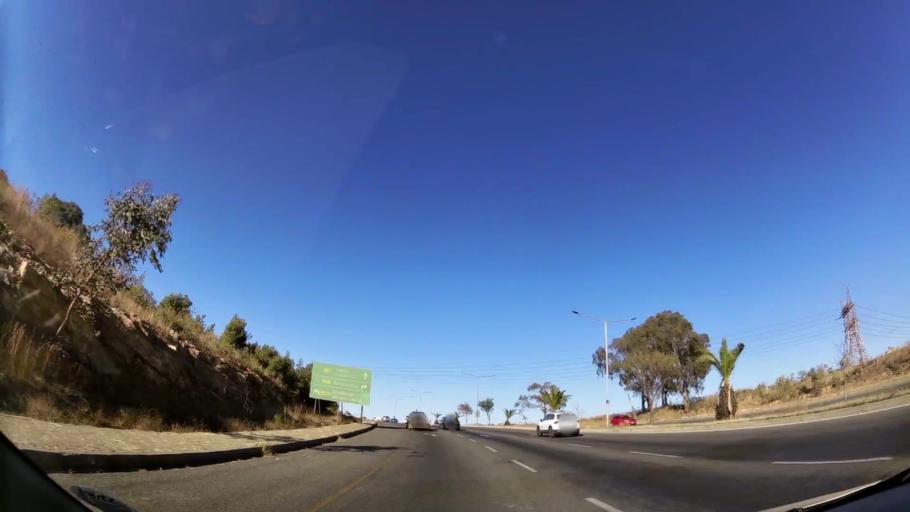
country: ZA
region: Gauteng
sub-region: West Rand District Municipality
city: Krugersdorp
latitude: -26.1121
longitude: 27.7760
